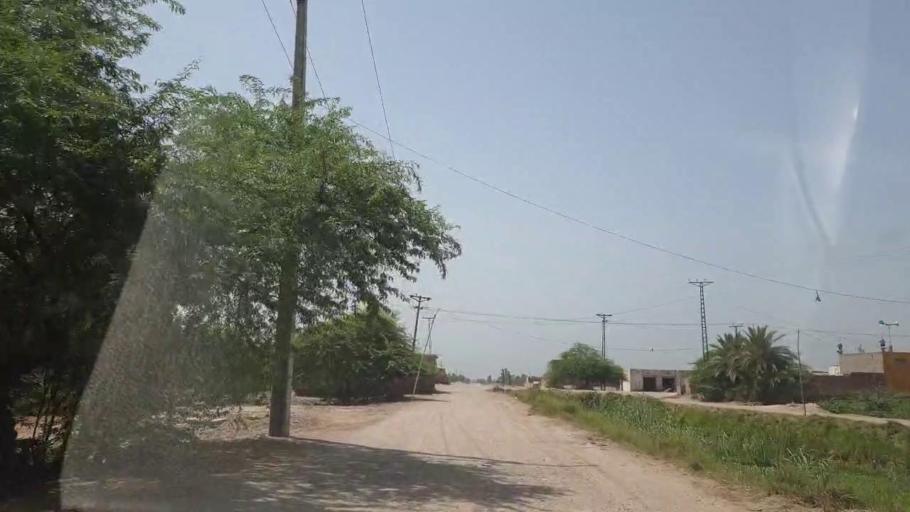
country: PK
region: Sindh
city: Ranipur
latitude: 27.2952
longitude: 68.5455
